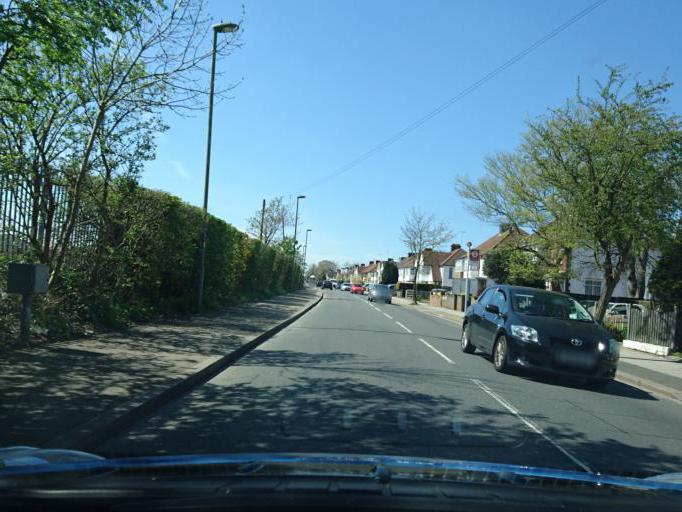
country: GB
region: England
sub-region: Greater London
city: Hendon
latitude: 51.6076
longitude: -0.1693
